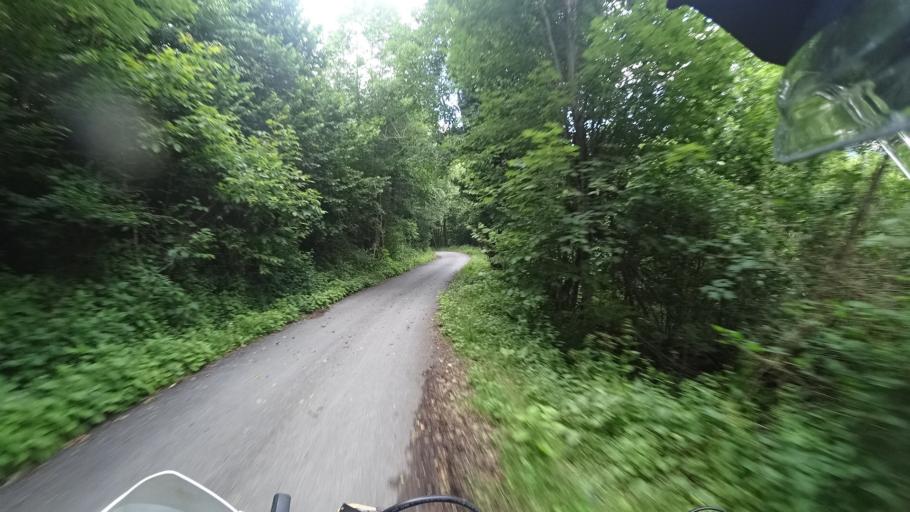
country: SI
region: Osilnica
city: Osilnica
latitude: 45.5207
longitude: 14.7259
